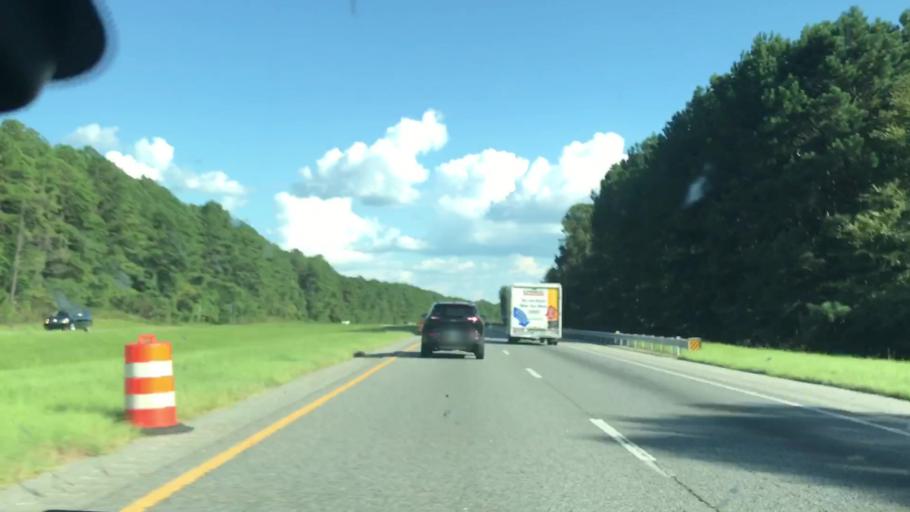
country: US
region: Georgia
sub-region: Harris County
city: Hamilton
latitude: 32.6274
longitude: -84.9587
